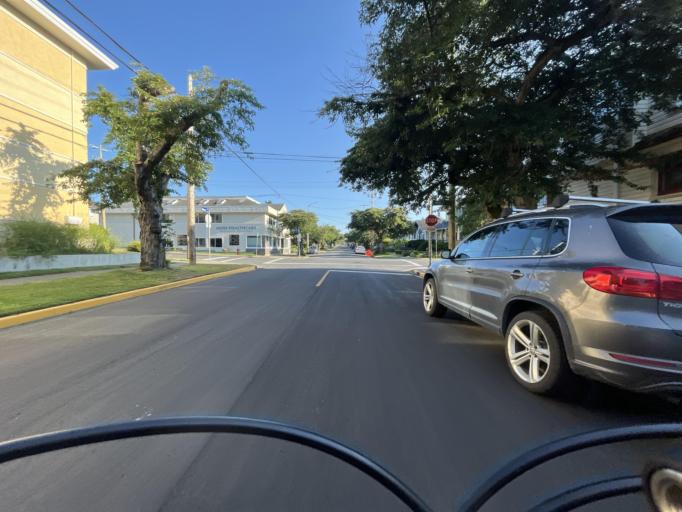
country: CA
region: British Columbia
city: Victoria
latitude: 48.4116
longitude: -123.3497
